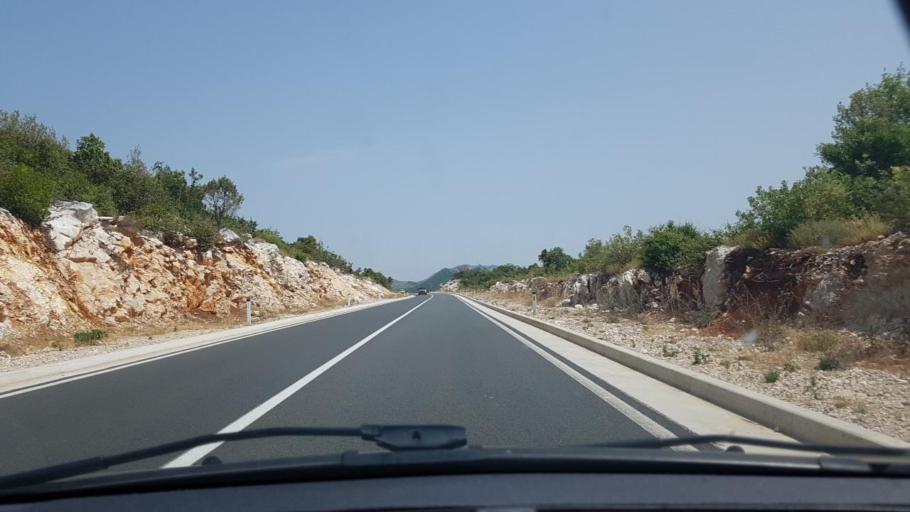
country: BA
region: Federation of Bosnia and Herzegovina
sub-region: Hercegovacko-Bosanski Kanton
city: Neum
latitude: 42.9577
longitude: 17.7240
